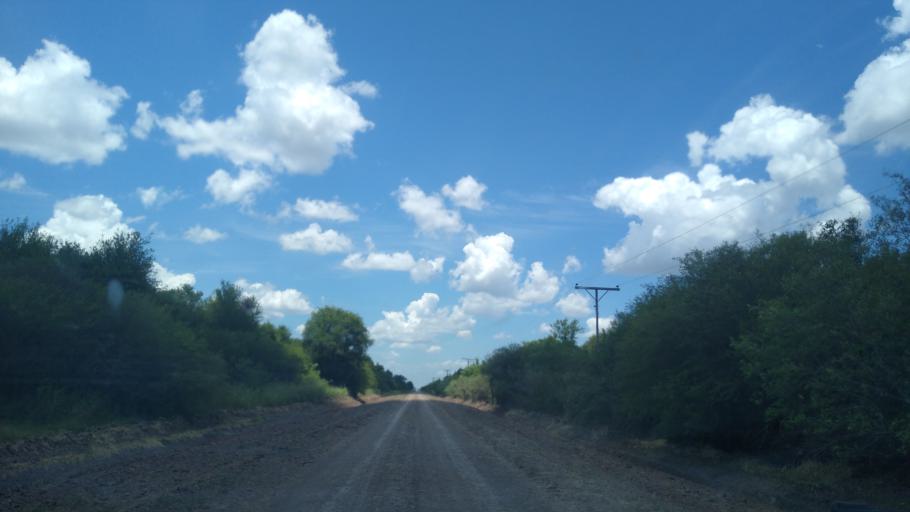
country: AR
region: Chaco
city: Presidencia Roque Saenz Pena
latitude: -26.7447
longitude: -60.3350
